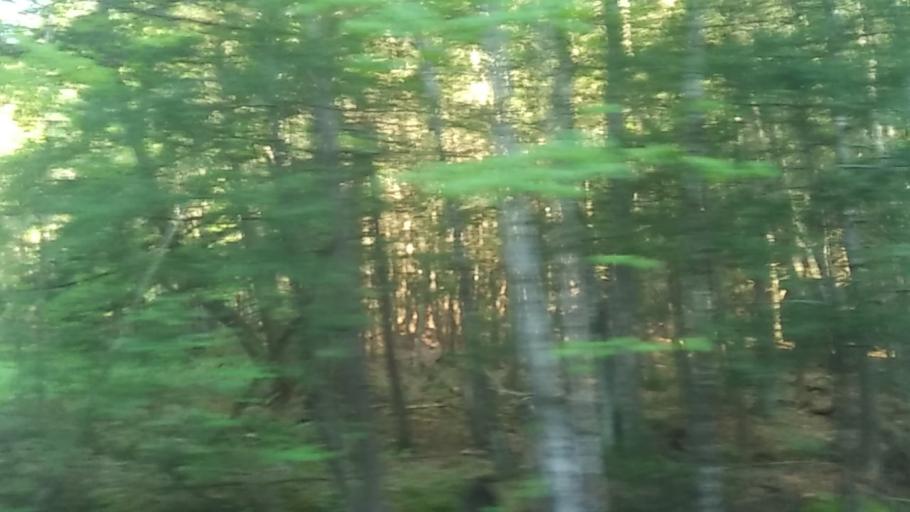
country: US
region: Massachusetts
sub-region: Franklin County
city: Buckland
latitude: 42.5768
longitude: -72.7734
